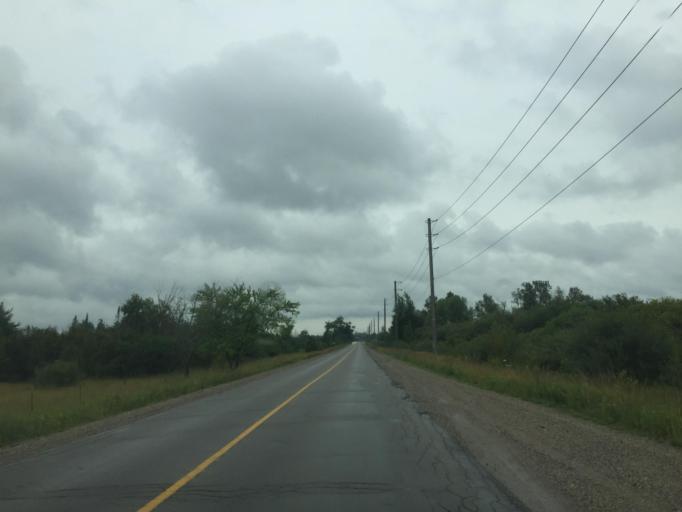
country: CA
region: Ontario
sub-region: Wellington County
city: Guelph
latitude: 43.4878
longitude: -80.2303
